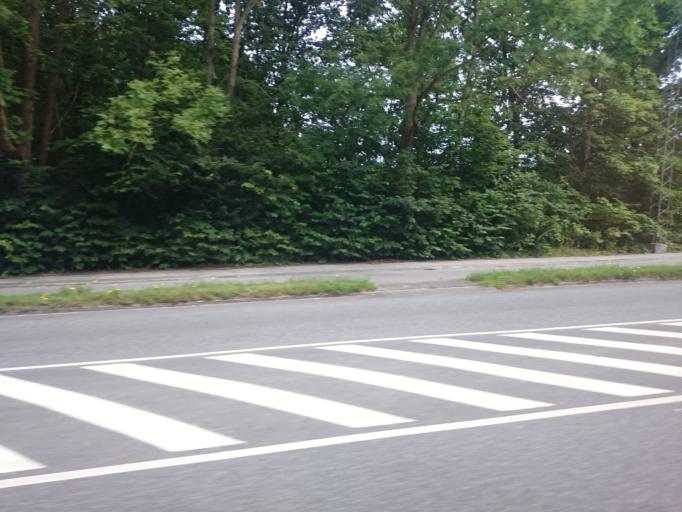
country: DK
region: Central Jutland
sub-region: Arhus Kommune
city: Arhus
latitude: 56.1343
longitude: 10.1900
